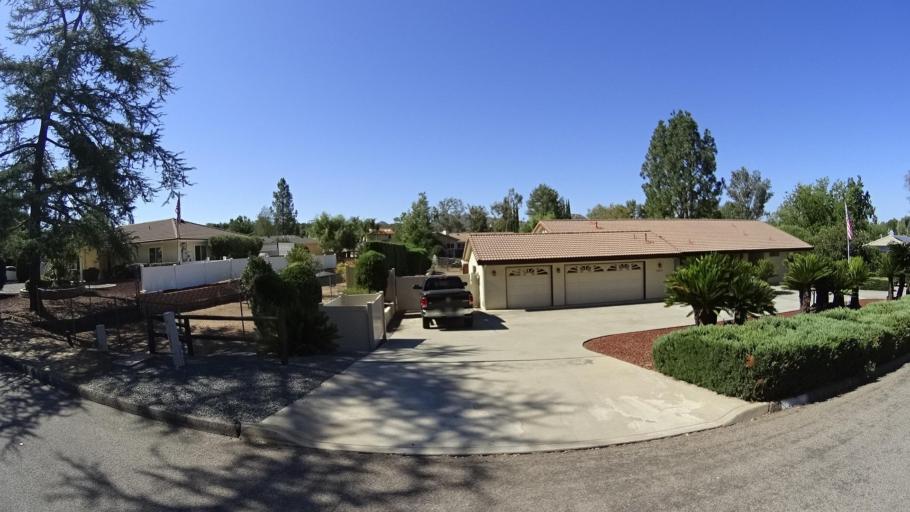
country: US
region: California
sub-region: San Diego County
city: San Diego Country Estates
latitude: 33.0076
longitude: -116.7808
